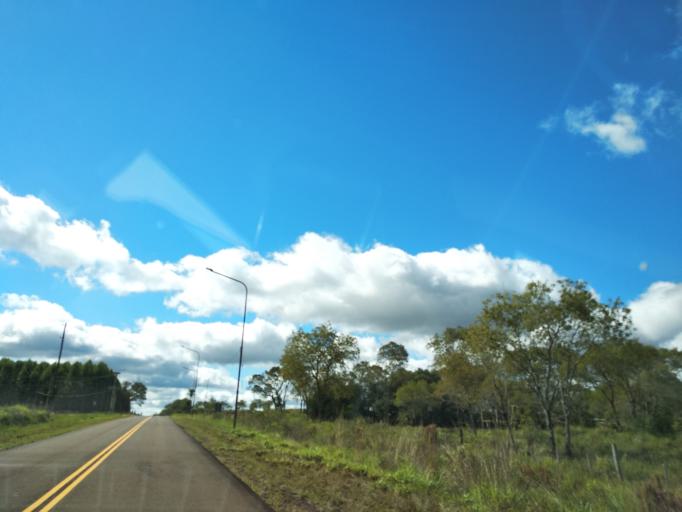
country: AR
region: Misiones
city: Santa Ana
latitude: -27.4089
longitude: -55.5542
